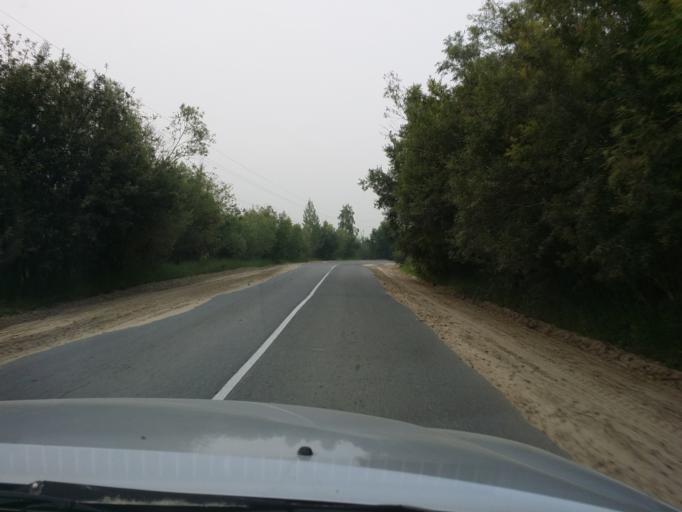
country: RU
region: Khanty-Mansiyskiy Avtonomnyy Okrug
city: Megion
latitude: 60.9964
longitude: 76.3016
